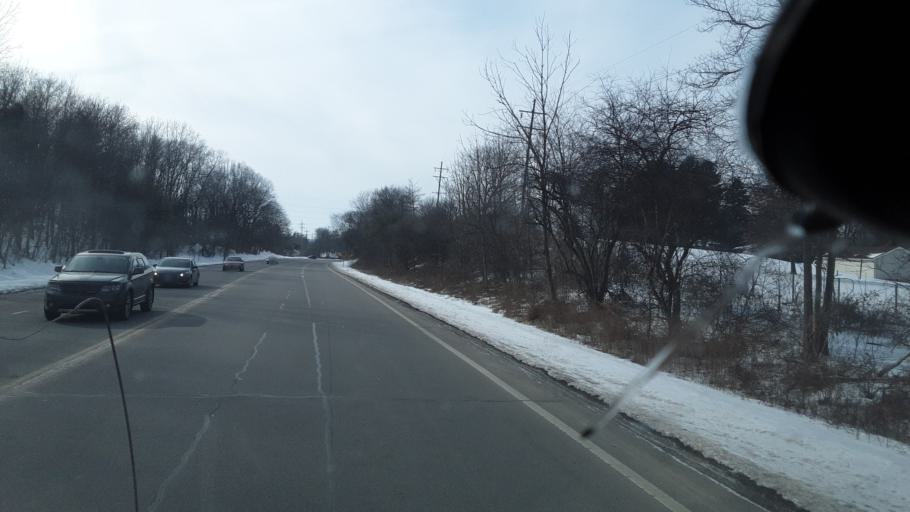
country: US
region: Ohio
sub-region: Summit County
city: Mogadore
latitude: 41.0301
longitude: -81.4142
